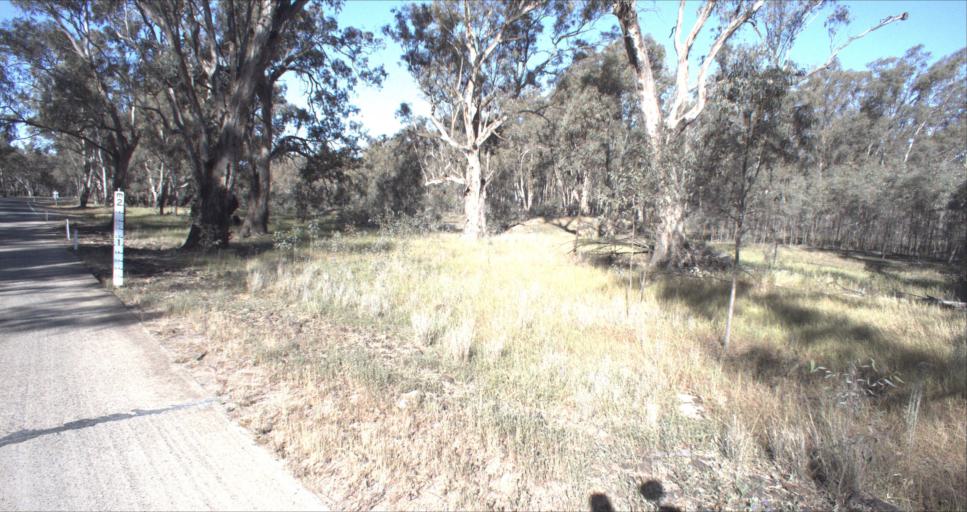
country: AU
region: New South Wales
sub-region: Leeton
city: Leeton
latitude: -34.6428
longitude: 146.3572
